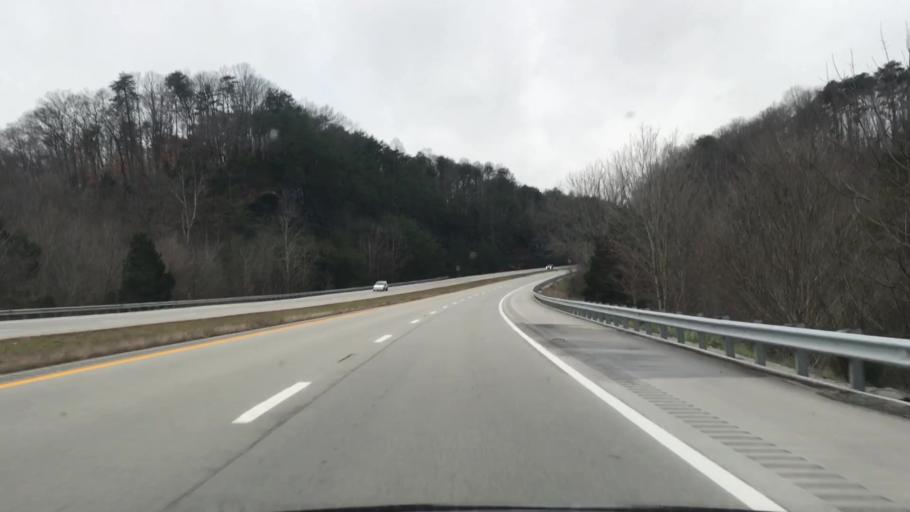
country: US
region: Kentucky
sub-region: Russell County
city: Jamestown
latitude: 37.0873
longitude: -84.8884
